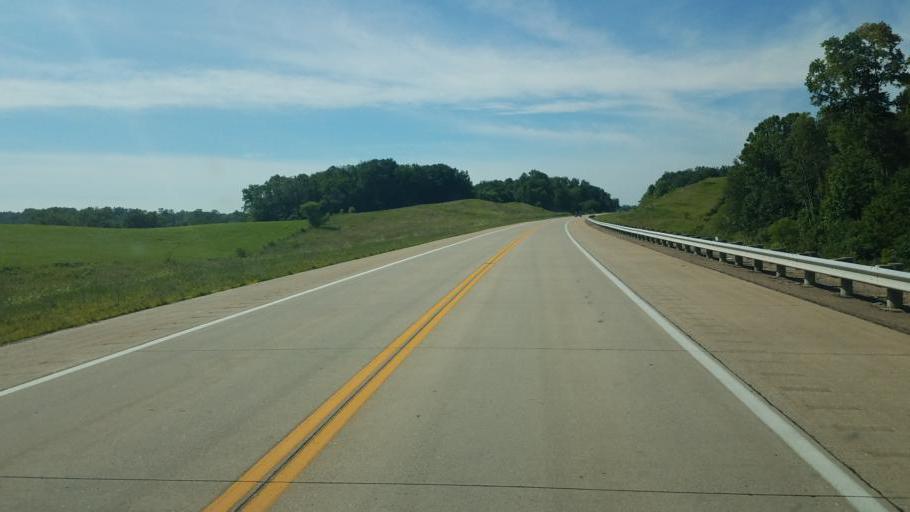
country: US
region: Ohio
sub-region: Meigs County
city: Pomeroy
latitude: 39.1540
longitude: -82.0323
